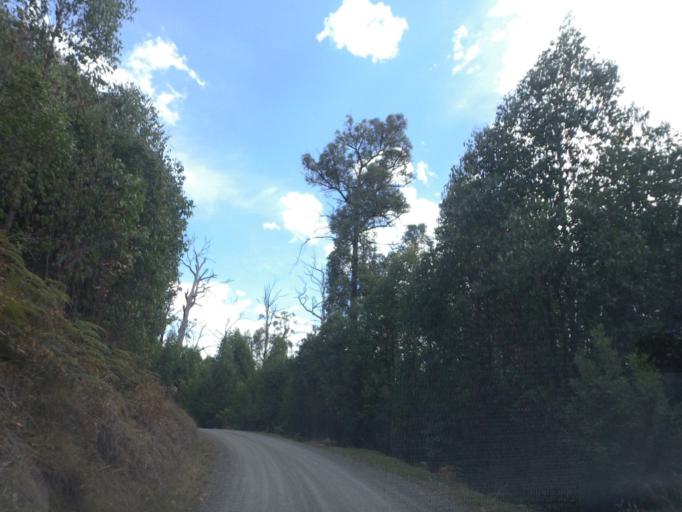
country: AU
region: Victoria
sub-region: Murrindindi
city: Alexandra
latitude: -37.4236
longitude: 145.7614
